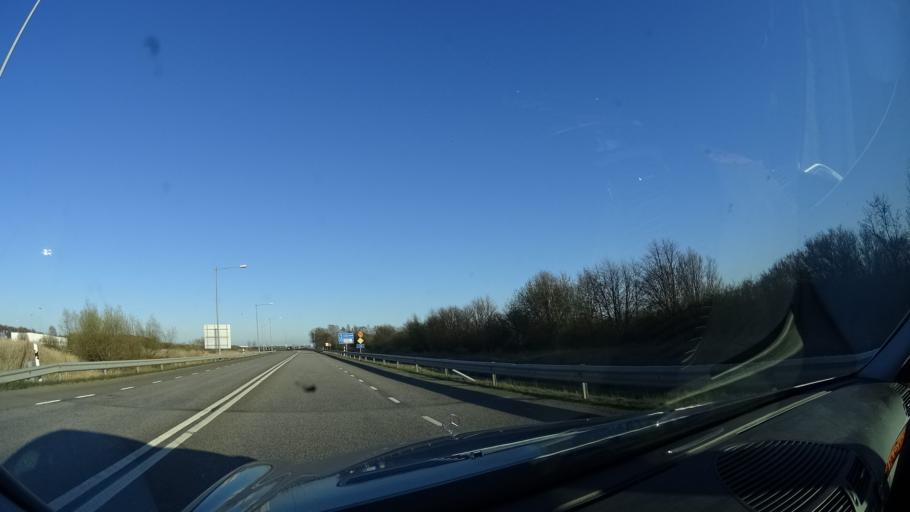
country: SE
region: Skane
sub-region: Helsingborg
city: Hyllinge
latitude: 56.0977
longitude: 12.8546
